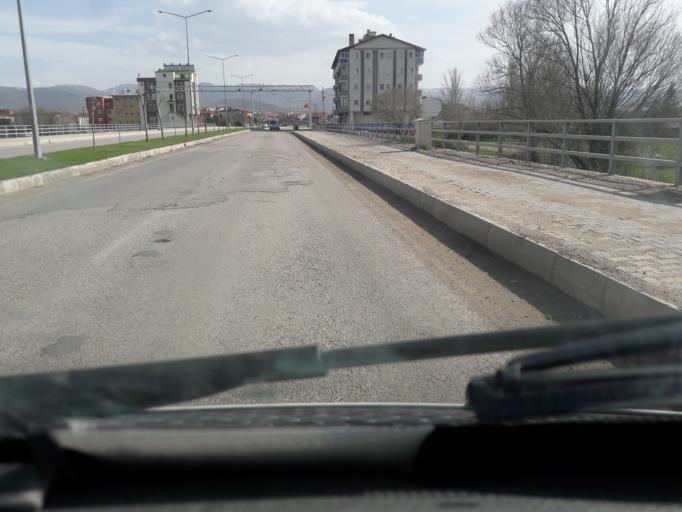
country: TR
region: Gumushane
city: Kelkit
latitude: 40.1402
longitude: 39.4334
